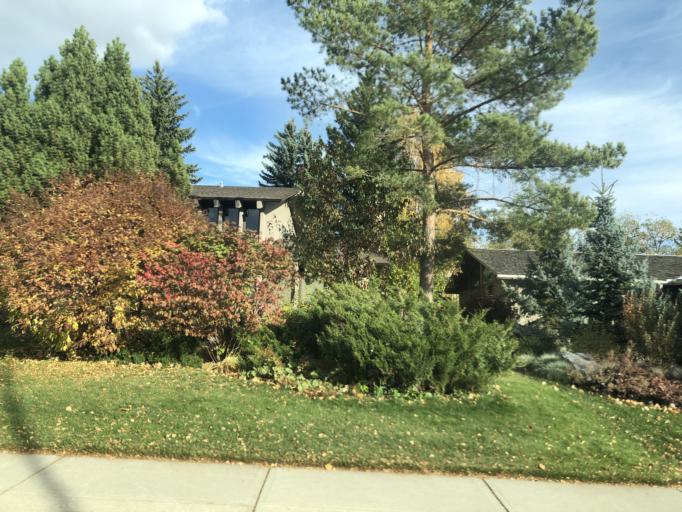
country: CA
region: Alberta
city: Calgary
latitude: 50.9320
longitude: -114.0594
